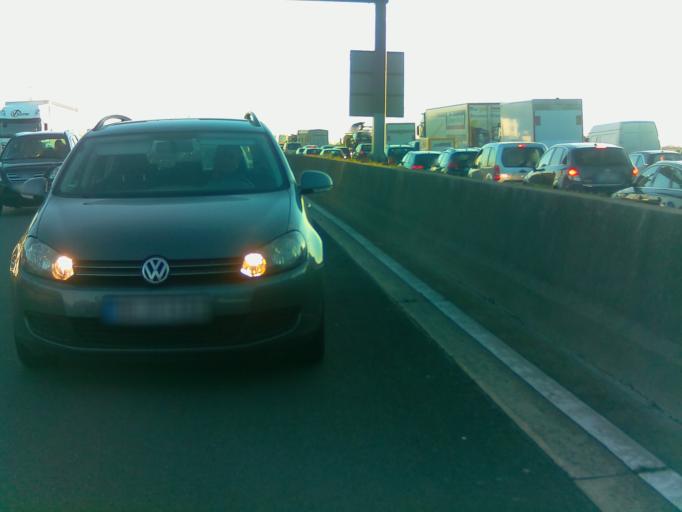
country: DE
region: Hesse
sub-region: Regierungsbezirk Darmstadt
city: Bad Homburg vor der Hoehe
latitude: 50.1837
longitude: 8.6181
